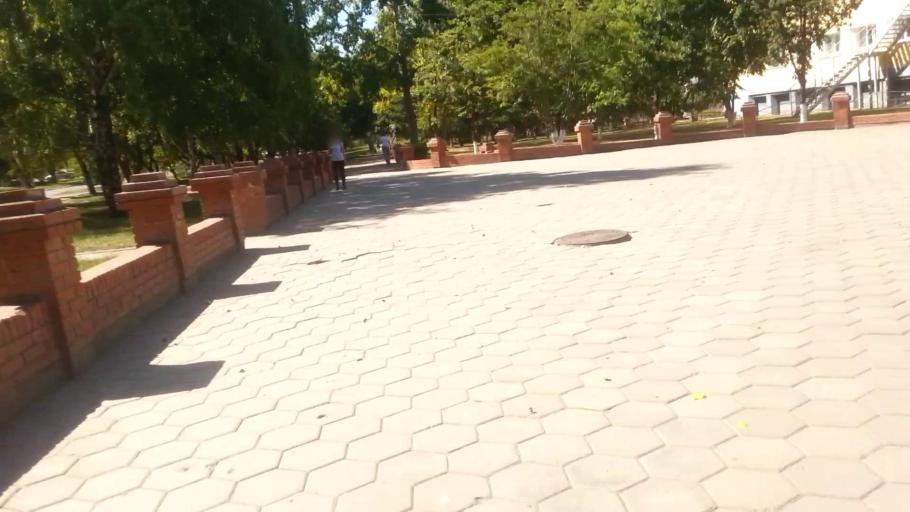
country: RU
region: Altai Krai
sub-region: Gorod Barnaulskiy
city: Barnaul
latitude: 53.3660
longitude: 83.6894
